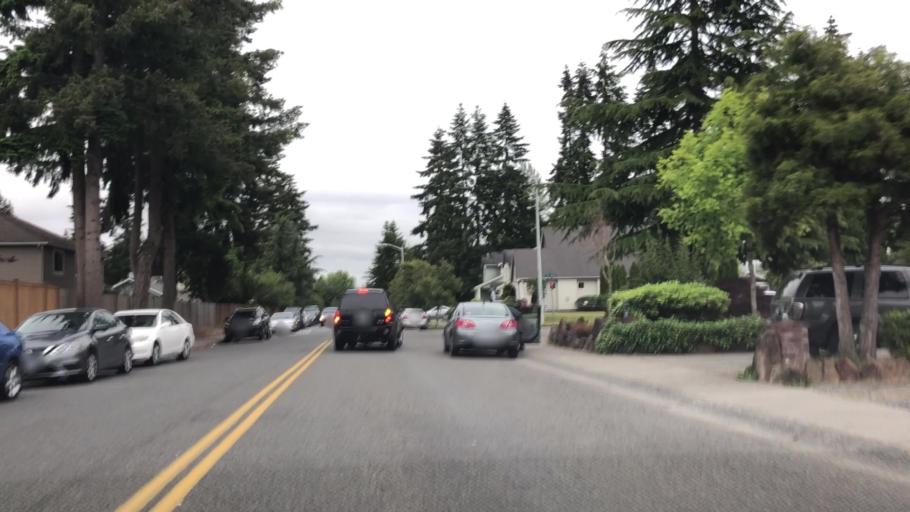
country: US
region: Washington
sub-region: Snohomish County
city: Mill Creek
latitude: 47.8746
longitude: -122.2022
